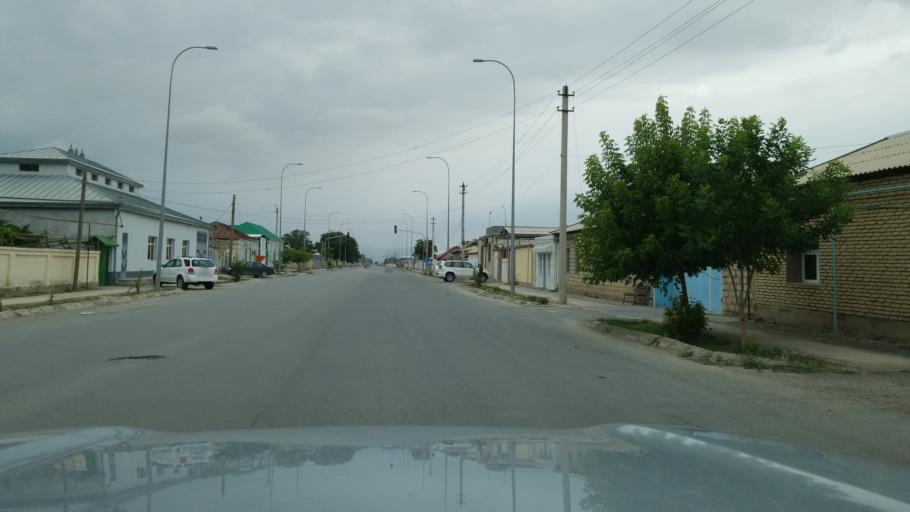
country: TM
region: Balkan
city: Serdar
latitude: 38.9760
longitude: 56.2661
